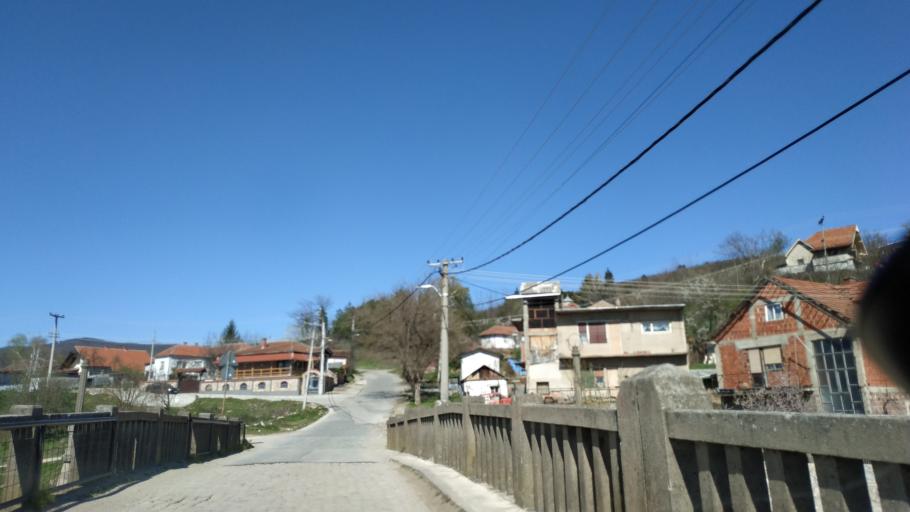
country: RS
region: Central Serbia
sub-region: Nisavski Okrug
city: Aleksinac
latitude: 43.5461
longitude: 21.7131
